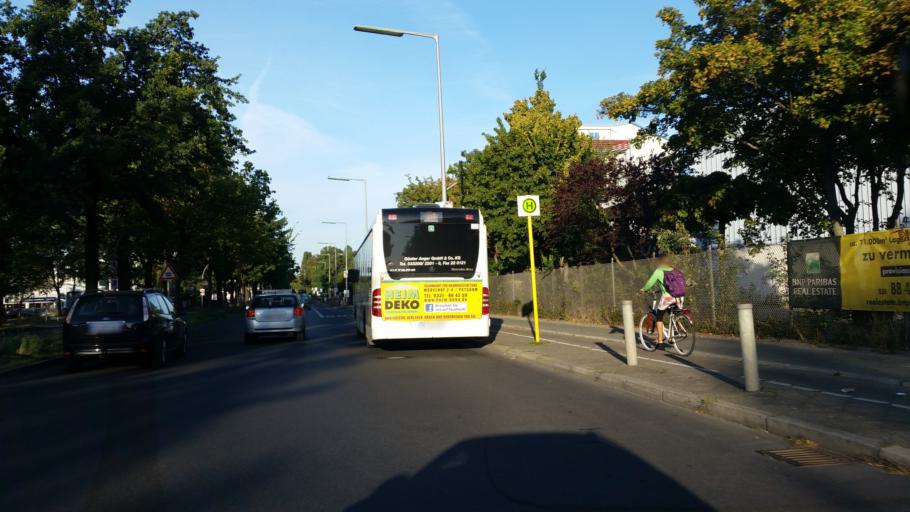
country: DE
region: Berlin
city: Marienfelde
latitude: 52.4118
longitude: 13.3864
